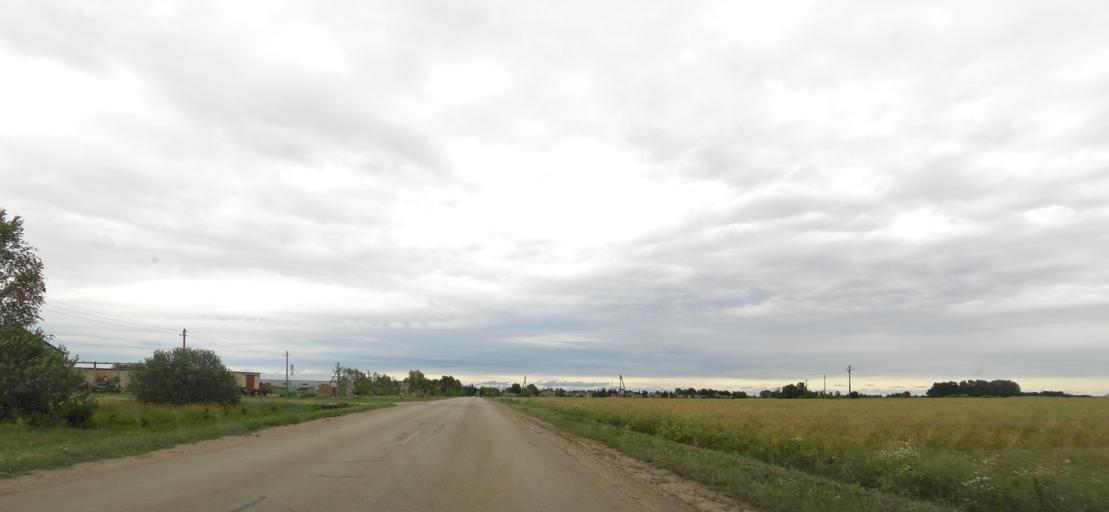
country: LT
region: Panevezys
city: Pasvalys
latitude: 56.0862
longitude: 24.5062
